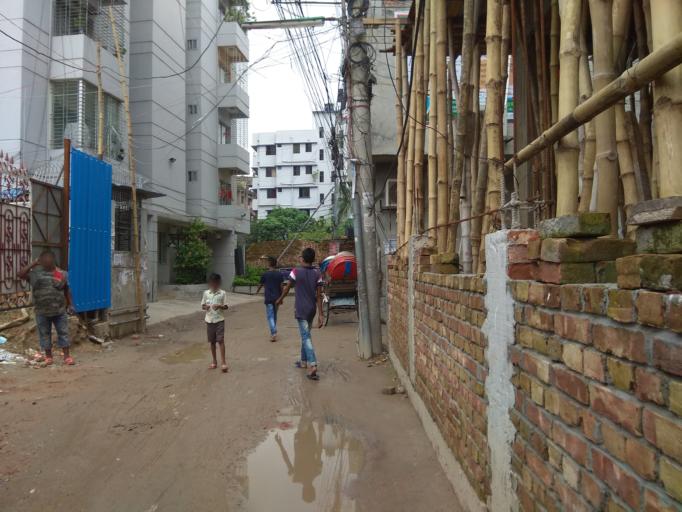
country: BD
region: Dhaka
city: Azimpur
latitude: 23.7955
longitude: 90.3706
